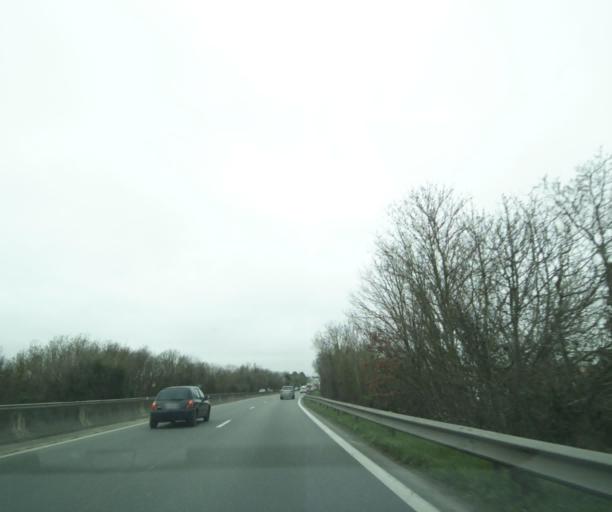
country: FR
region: Poitou-Charentes
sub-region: Departement de la Charente-Maritime
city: Puilboreau
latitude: 46.1636
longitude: -1.1220
